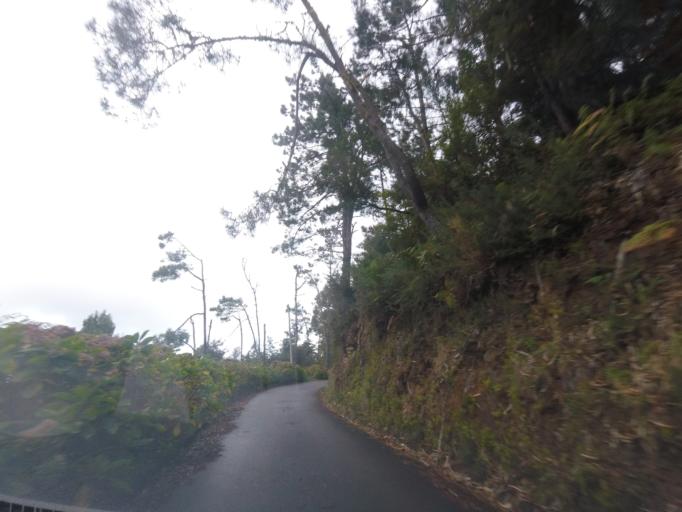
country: PT
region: Madeira
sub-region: Santana
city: Santana
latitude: 32.7955
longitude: -16.8923
